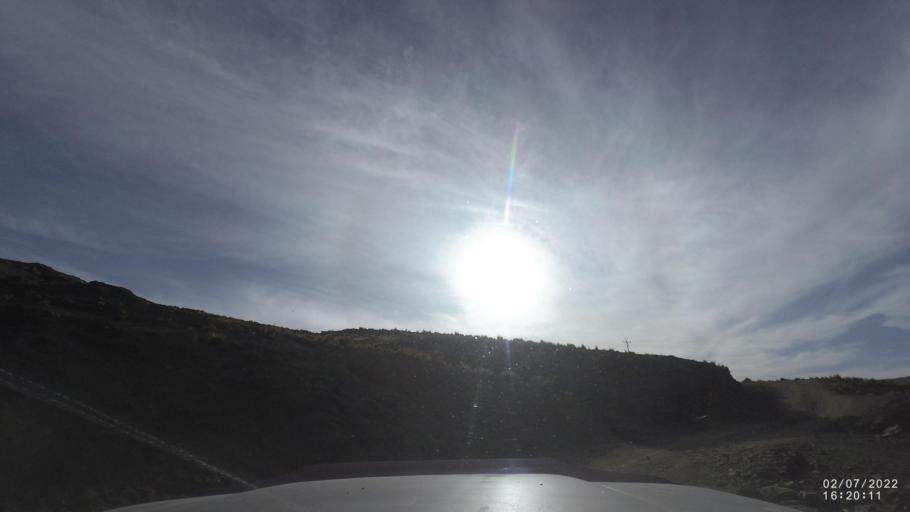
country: BO
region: Cochabamba
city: Irpa Irpa
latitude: -17.9313
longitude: -66.4467
